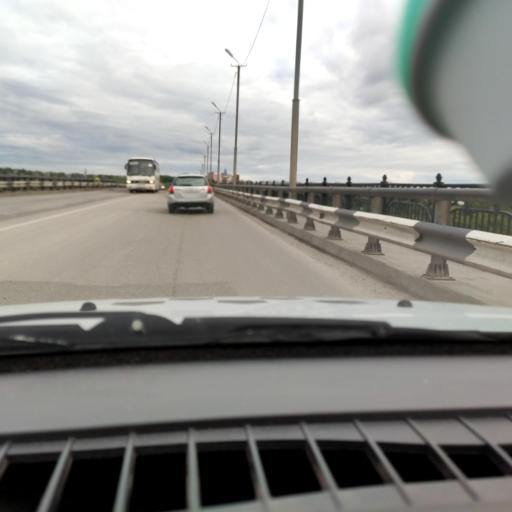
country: RU
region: Perm
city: Chusovoy
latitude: 58.2875
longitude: 57.8123
